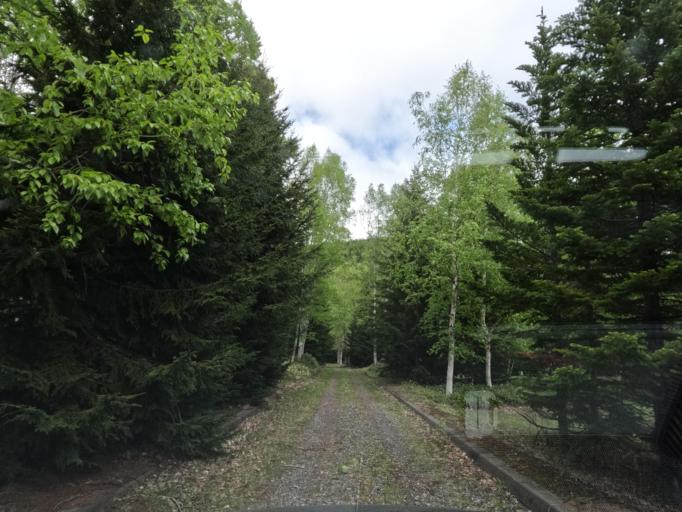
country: JP
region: Hokkaido
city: Kamikawa
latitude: 43.6431
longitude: 143.0225
